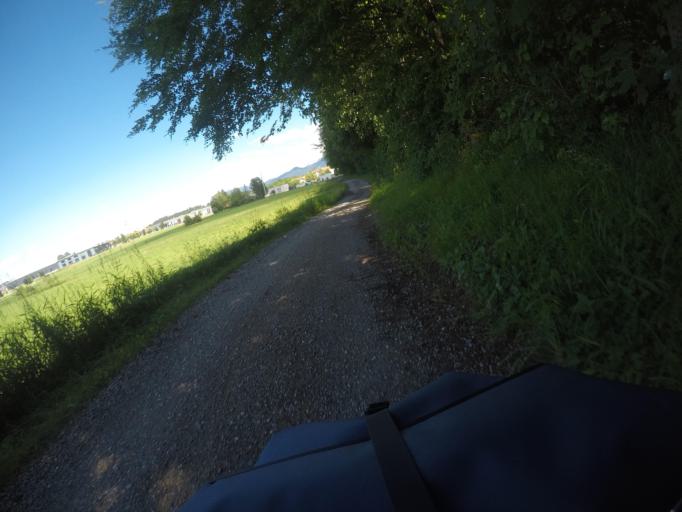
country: AT
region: Tyrol
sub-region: Politischer Bezirk Reutte
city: Vils
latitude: 47.5682
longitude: 10.6632
